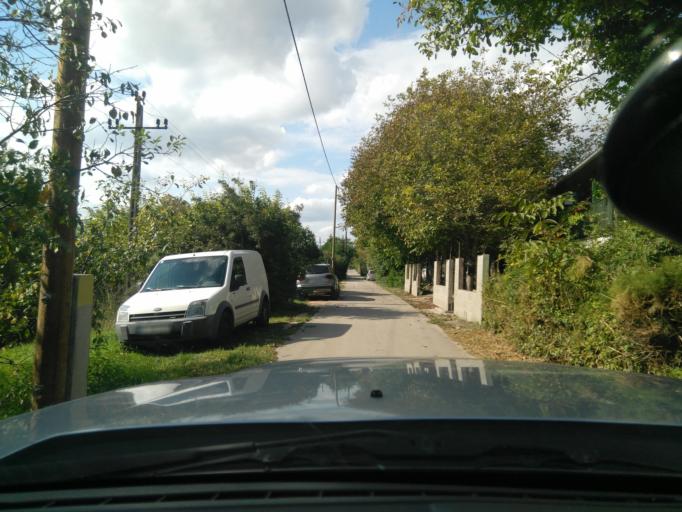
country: HU
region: Fejer
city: Bicske
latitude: 47.4958
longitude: 18.6466
